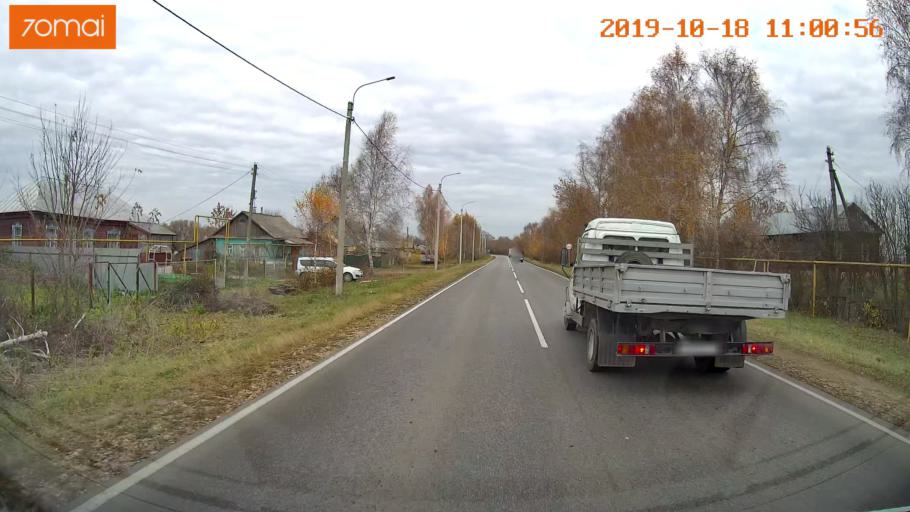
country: RU
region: Tula
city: Yepifan'
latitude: 53.8487
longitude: 38.5527
